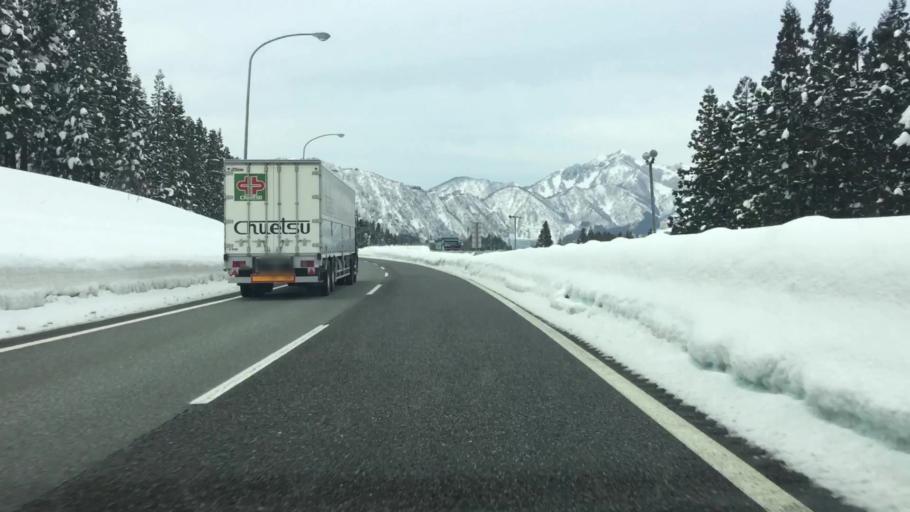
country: JP
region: Niigata
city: Shiozawa
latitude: 36.8903
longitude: 138.8478
